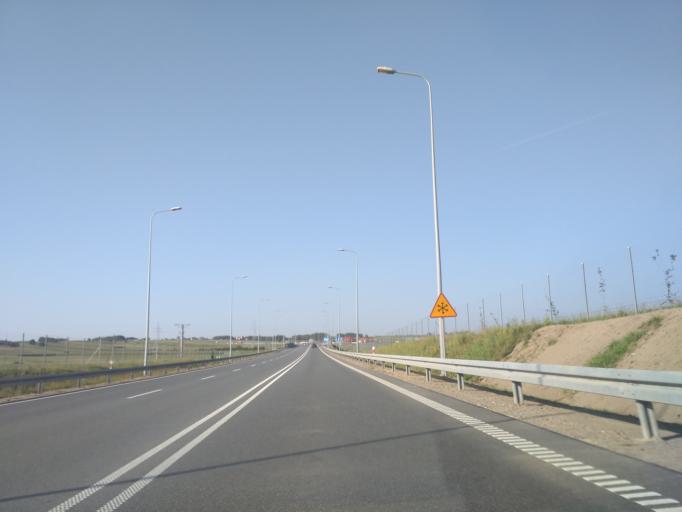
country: PL
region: Subcarpathian Voivodeship
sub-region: Powiat rzeszowski
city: Sokolow Malopolski
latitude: 50.2091
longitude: 22.1151
